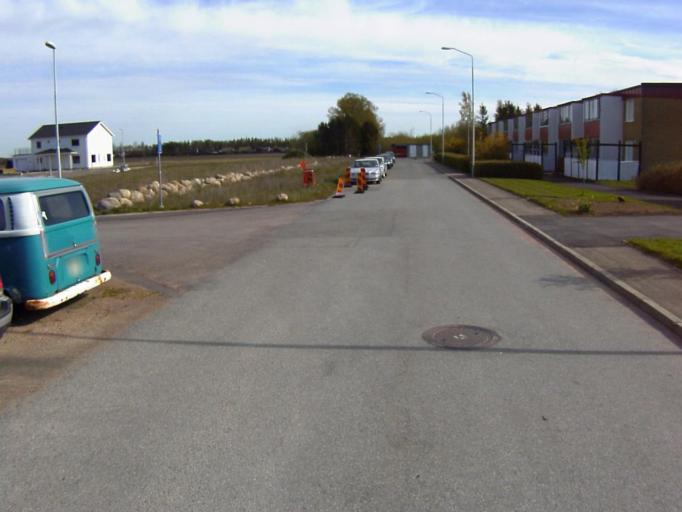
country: SE
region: Skane
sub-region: Kristianstads Kommun
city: Norra Asum
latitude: 55.9941
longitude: 14.1451
